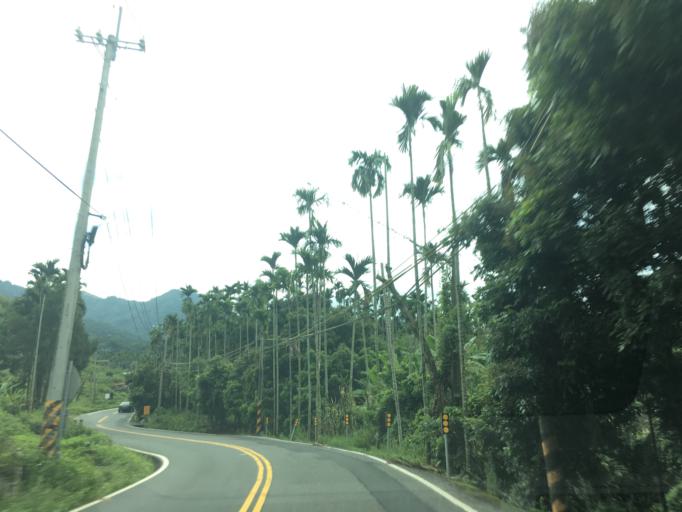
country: TW
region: Taiwan
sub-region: Yunlin
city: Douliu
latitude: 23.5687
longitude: 120.5670
